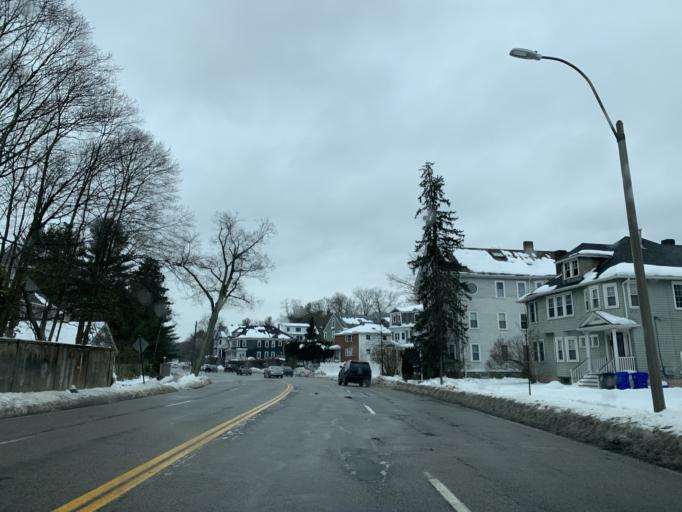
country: US
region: Massachusetts
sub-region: Norfolk County
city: Brookline
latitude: 42.3217
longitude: -71.1631
